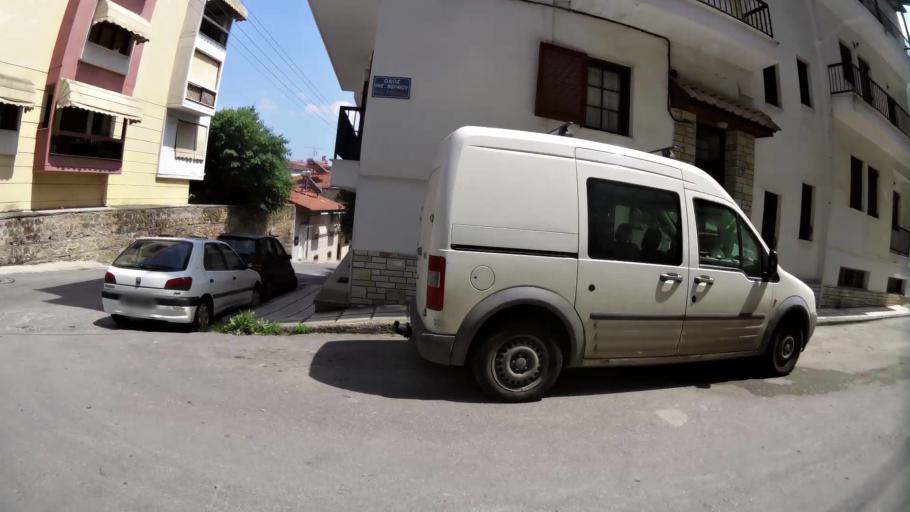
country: GR
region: Central Macedonia
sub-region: Nomos Imathias
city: Veroia
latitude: 40.5189
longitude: 22.2022
